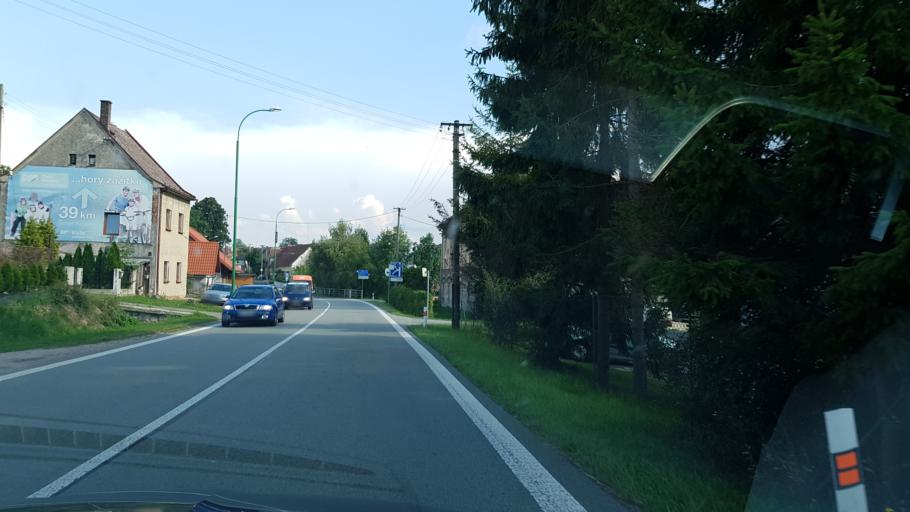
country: CZ
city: Vamberk
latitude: 50.1100
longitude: 16.3635
